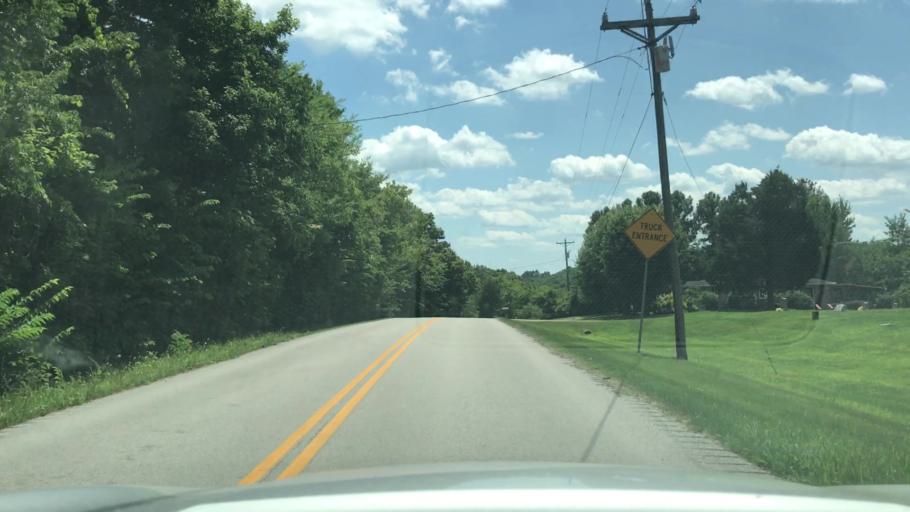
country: US
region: Kentucky
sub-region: Hopkins County
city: Nortonville
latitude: 37.0975
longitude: -87.3410
